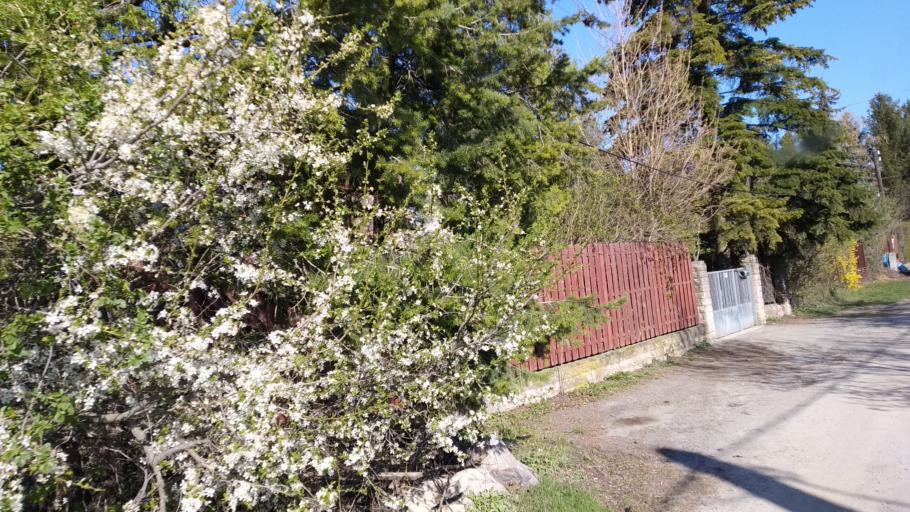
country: HU
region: Pest
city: Leanyfalu
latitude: 47.7095
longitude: 19.0809
